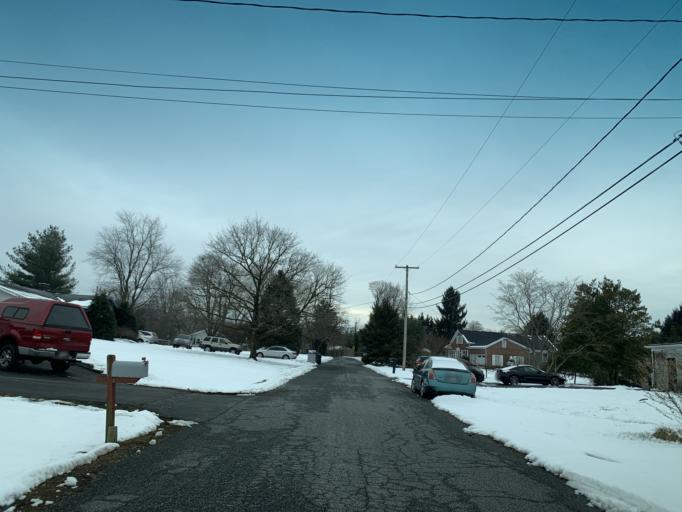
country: US
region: Maryland
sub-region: Harford County
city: Bel Air North
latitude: 39.5769
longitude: -76.3576
